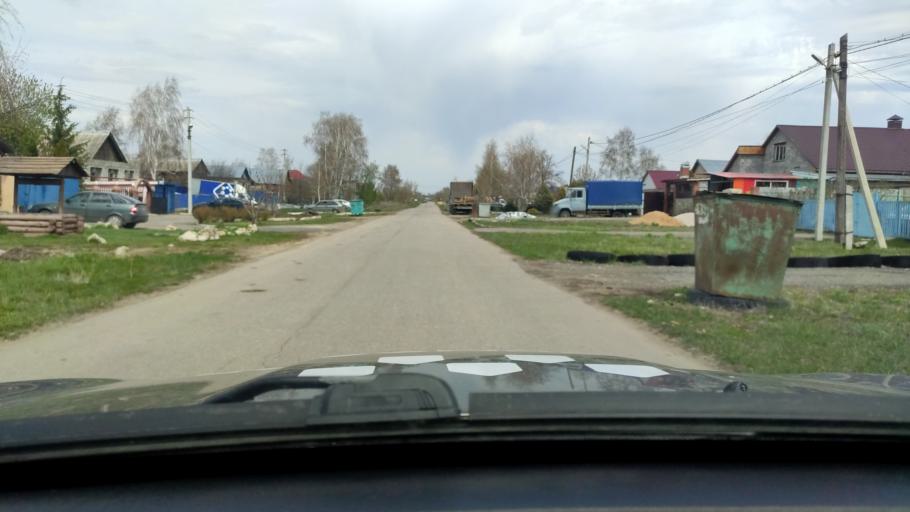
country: RU
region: Samara
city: Tol'yatti
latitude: 53.5592
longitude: 49.3984
